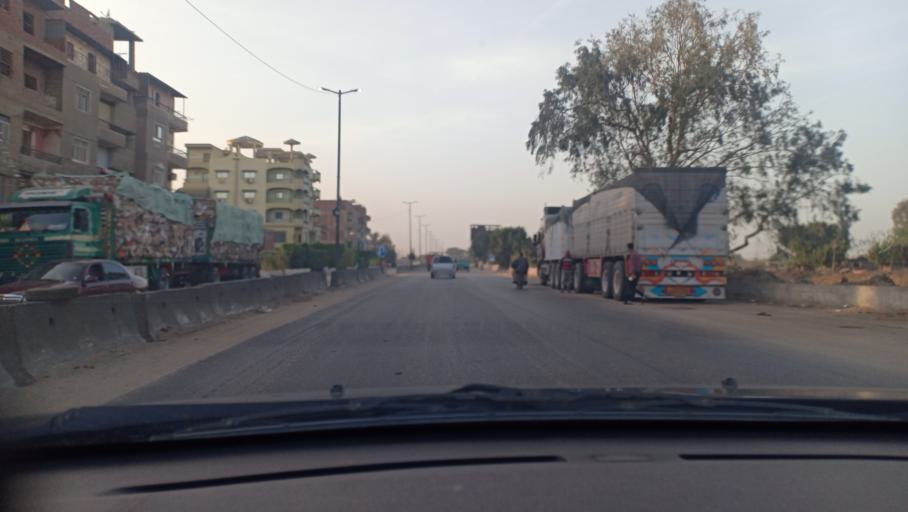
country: EG
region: Muhafazat al Minufiyah
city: Quwaysina
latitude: 30.5782
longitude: 31.2735
